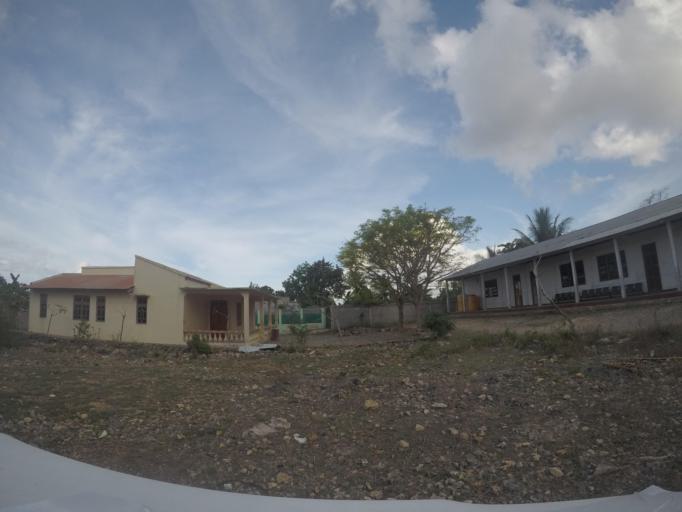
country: TL
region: Baucau
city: Baucau
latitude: -8.4791
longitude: 126.4569
